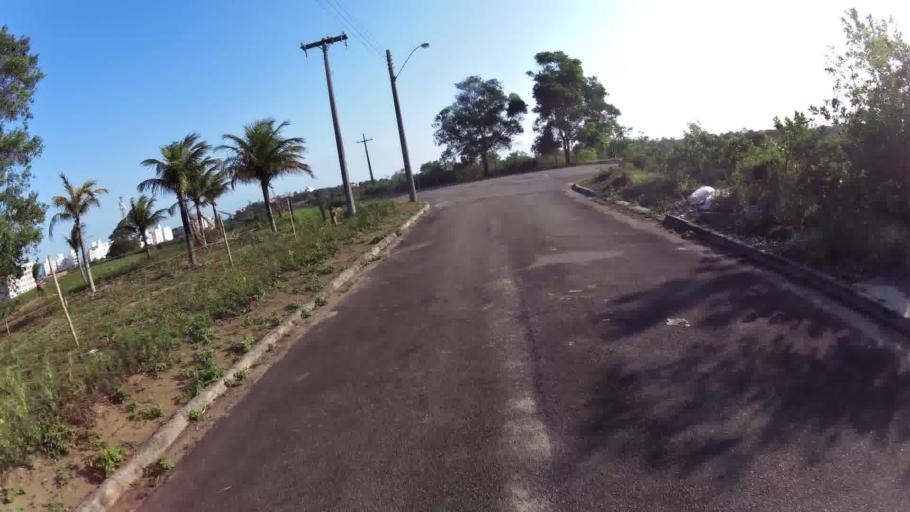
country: BR
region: Espirito Santo
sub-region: Guarapari
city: Guarapari
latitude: -20.7281
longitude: -40.5334
